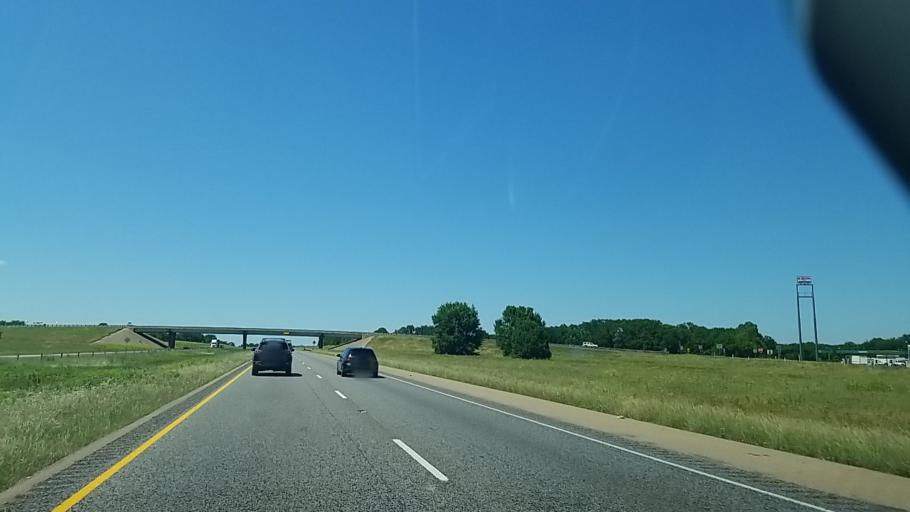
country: US
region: Texas
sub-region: Freestone County
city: Fairfield
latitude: 31.5951
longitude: -96.1532
